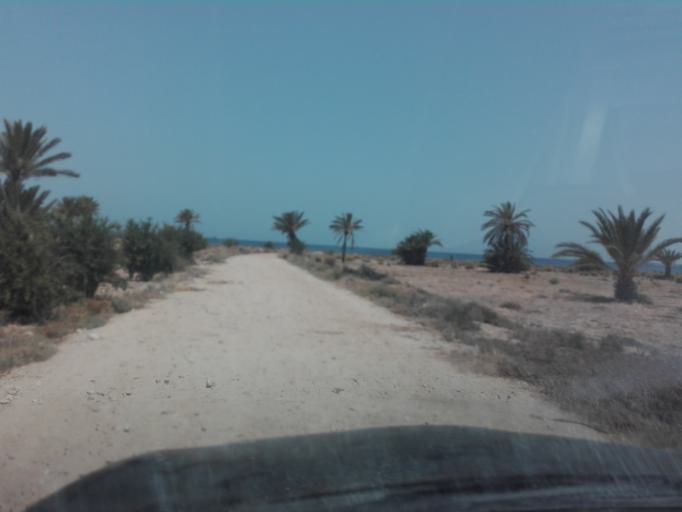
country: TN
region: Safaqis
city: Al Qarmadah
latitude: 34.6672
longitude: 11.0932
